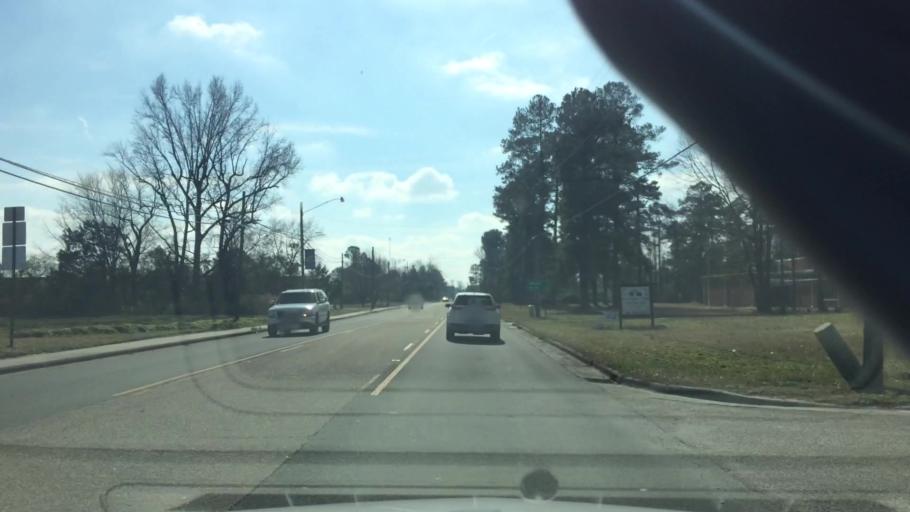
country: US
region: North Carolina
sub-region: Duplin County
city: Beulaville
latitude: 34.9209
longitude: -77.7744
